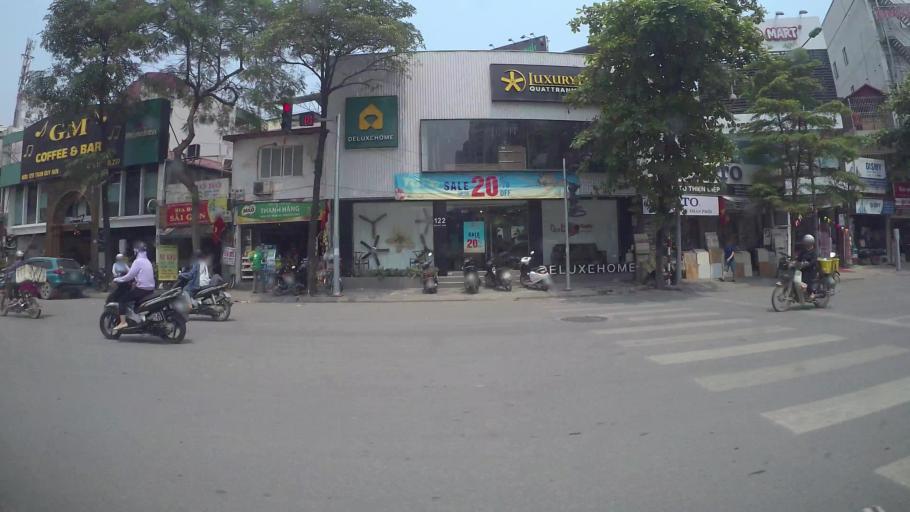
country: VN
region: Ha Noi
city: Thanh Xuan
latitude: 21.0106
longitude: 105.7994
